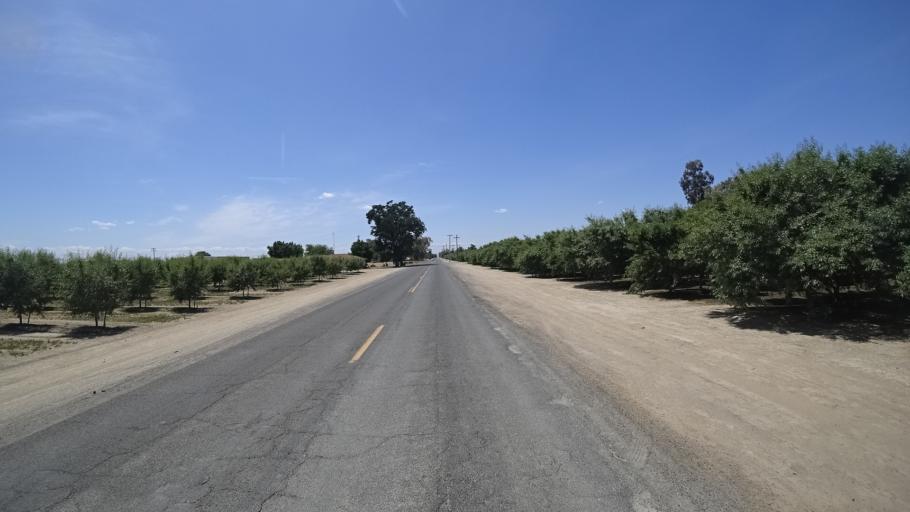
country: US
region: California
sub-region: Kings County
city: Lemoore
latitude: 36.2837
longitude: -119.7613
